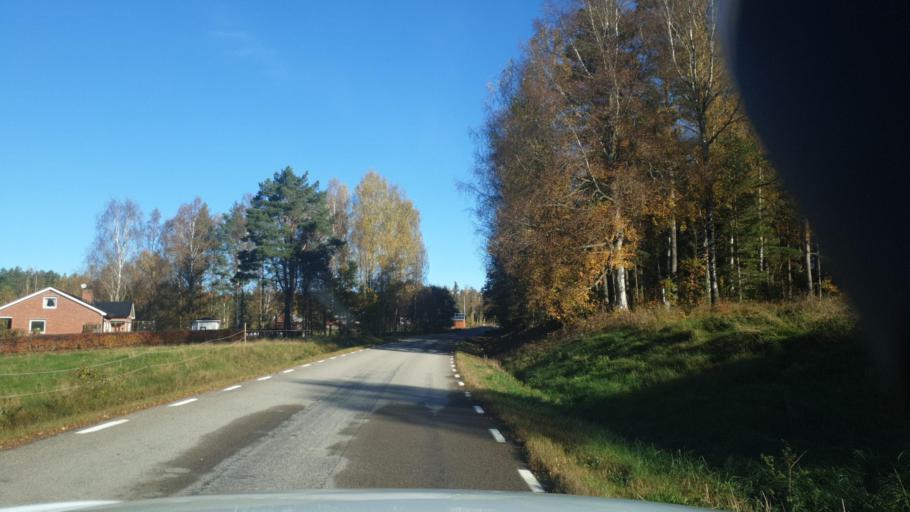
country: SE
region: Vaermland
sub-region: Arvika Kommun
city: Arvika
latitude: 59.5524
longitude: 12.7411
